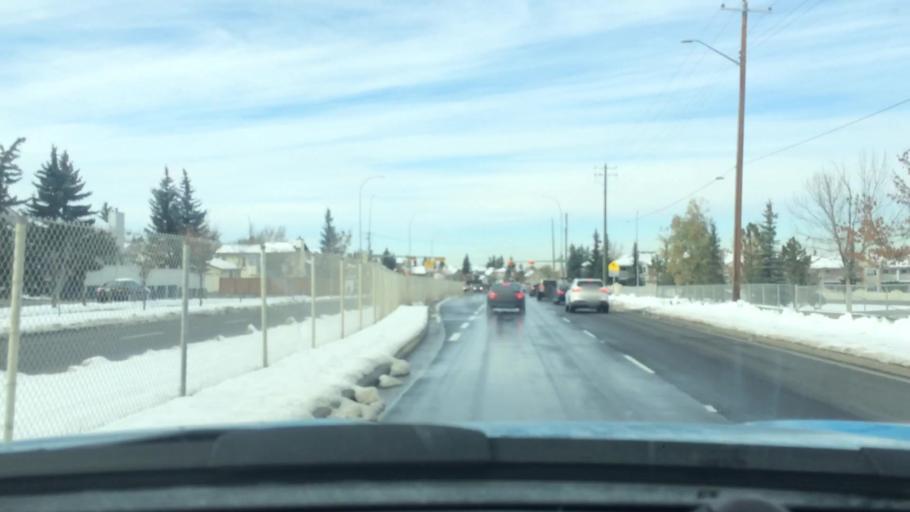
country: CA
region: Alberta
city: Calgary
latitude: 51.1390
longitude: -114.1083
